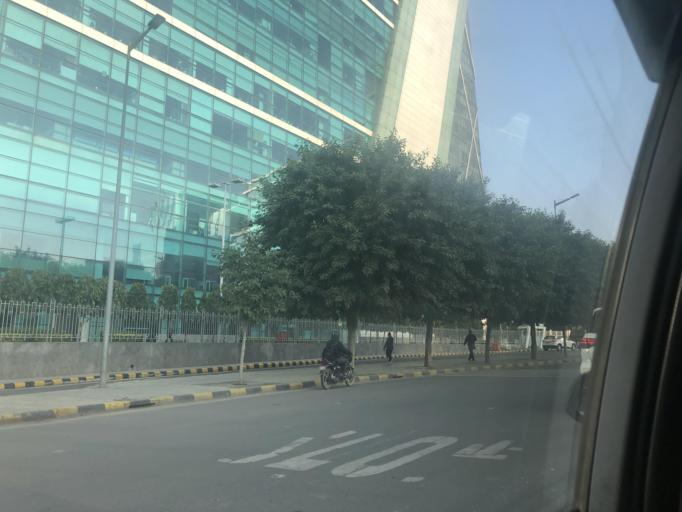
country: IN
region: Haryana
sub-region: Gurgaon
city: Gurgaon
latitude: 28.4963
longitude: 77.0922
